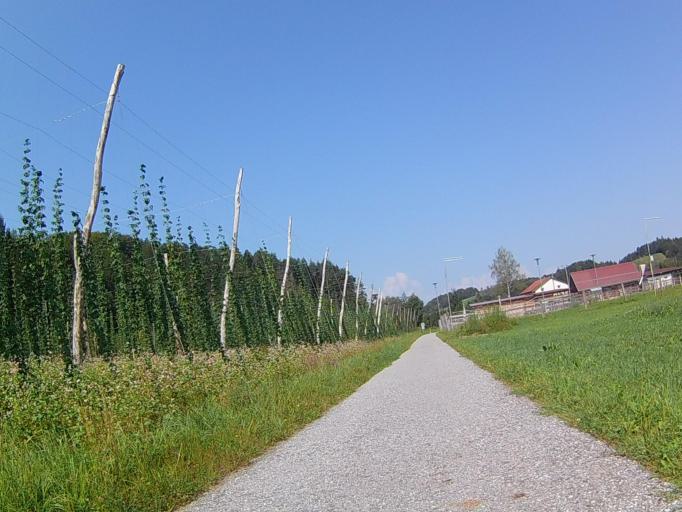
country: AT
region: Styria
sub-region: Politischer Bezirk Leibnitz
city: Leutschach
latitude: 46.6646
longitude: 15.4569
